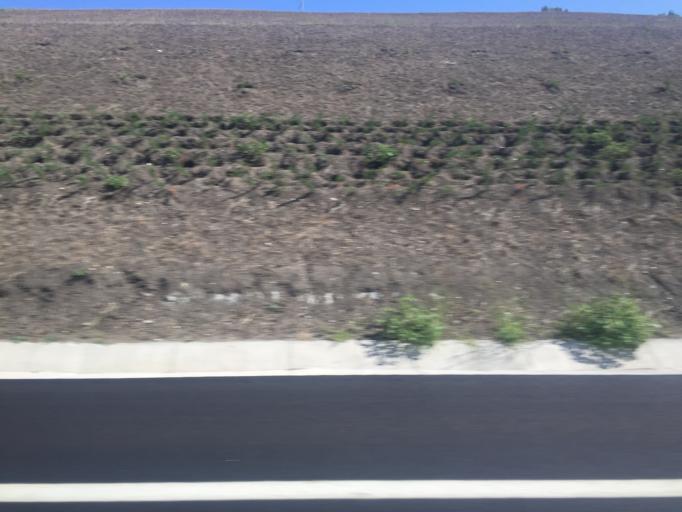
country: TR
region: Bursa
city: Gorukle
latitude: 40.2463
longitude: 28.7565
